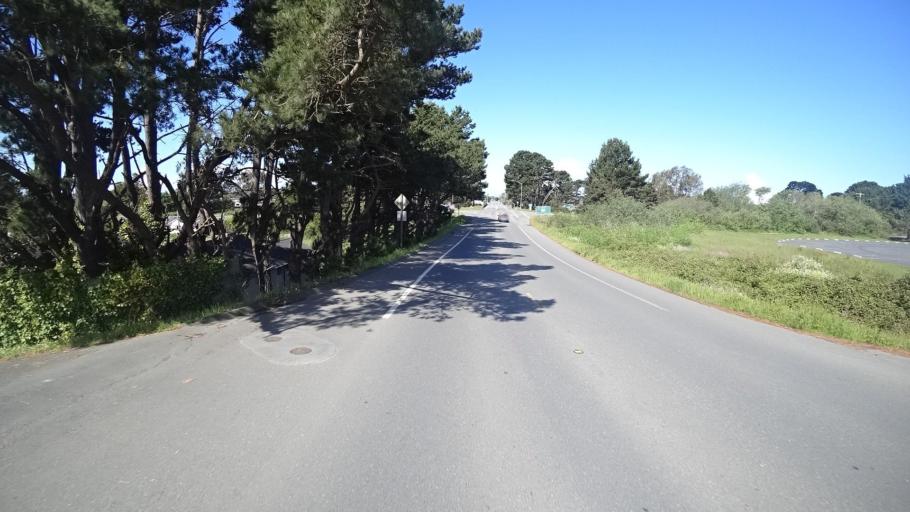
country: US
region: California
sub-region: Humboldt County
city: McKinleyville
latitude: 40.9343
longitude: -124.1132
